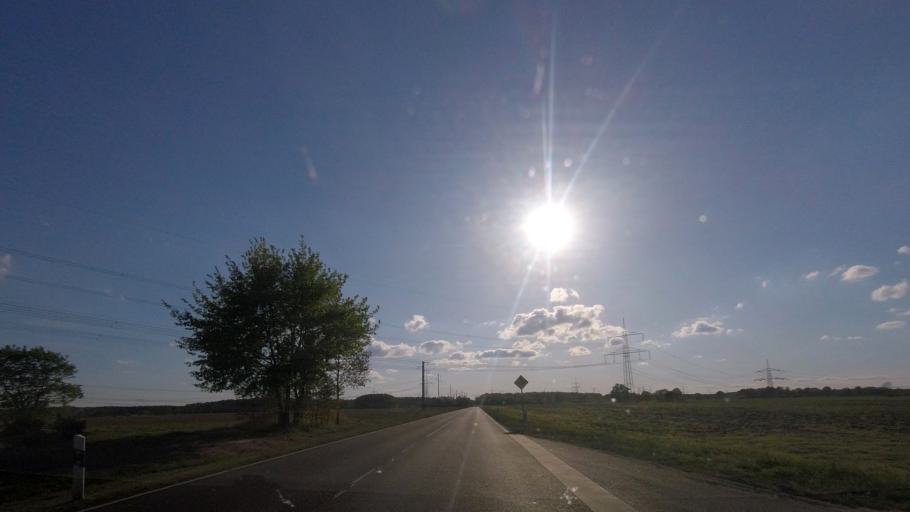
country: DE
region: Brandenburg
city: Luebben
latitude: 51.9056
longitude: 13.8516
